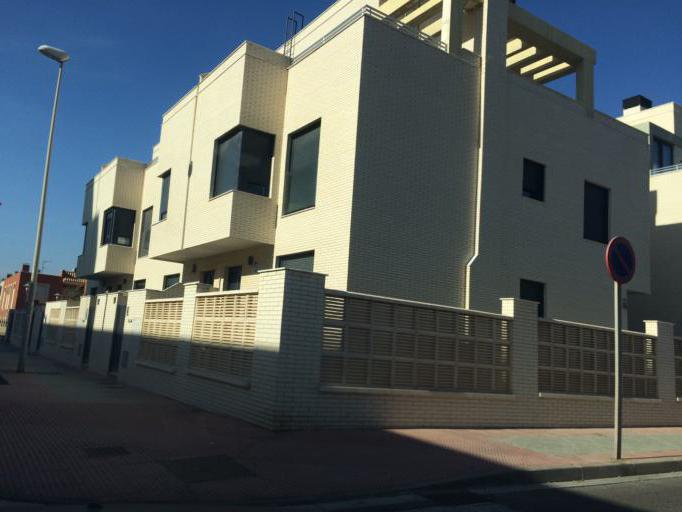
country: ES
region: Andalusia
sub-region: Provincia de Almeria
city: Almeria
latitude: 36.8240
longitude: -2.4412
